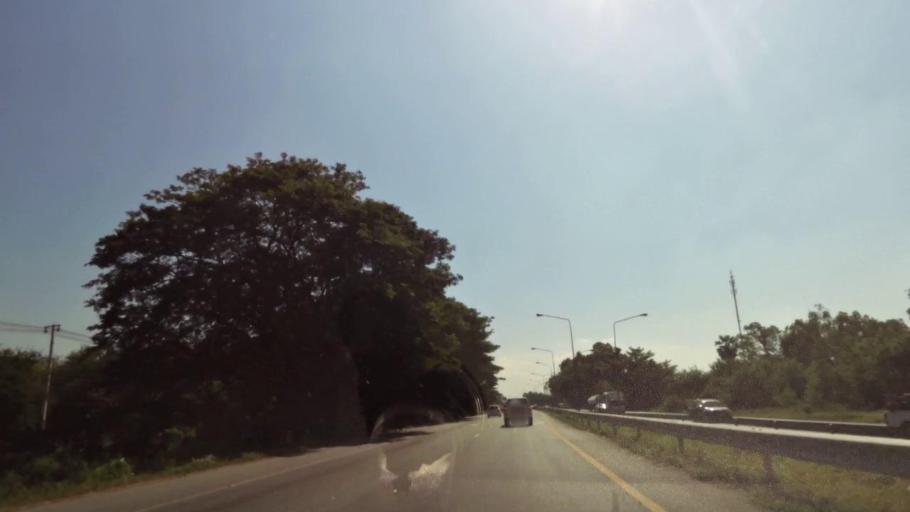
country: TH
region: Nakhon Sawan
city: Kao Liao
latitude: 15.7835
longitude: 100.1211
